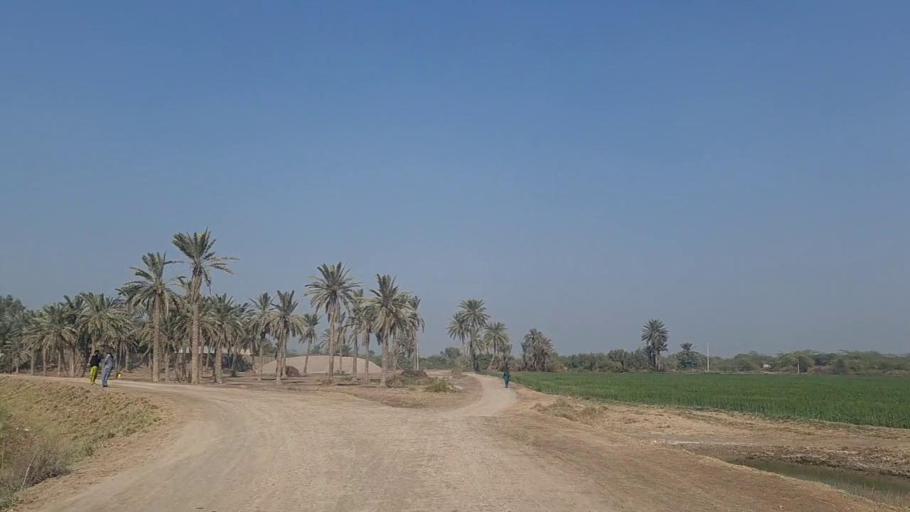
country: PK
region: Sindh
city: Nawabshah
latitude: 26.2343
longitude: 68.4940
